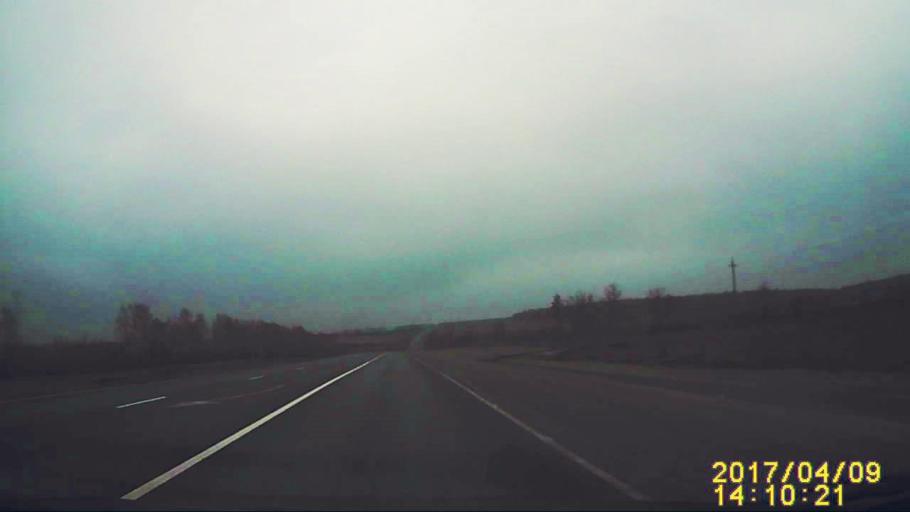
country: RU
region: Ulyanovsk
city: Krasnyy Gulyay
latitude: 54.0375
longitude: 48.2132
